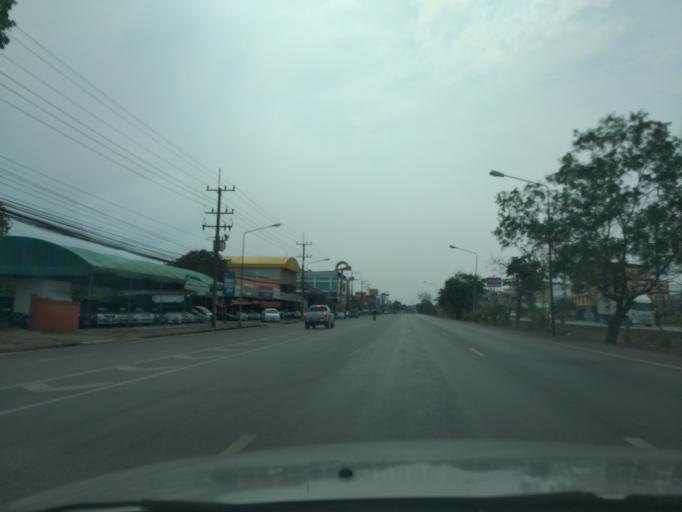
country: TH
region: Rayong
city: Klaeng
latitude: 12.7863
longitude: 101.6694
